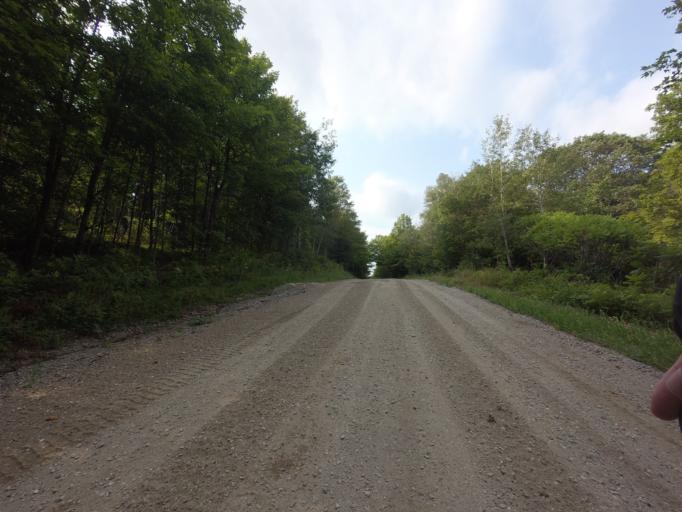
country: CA
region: Ontario
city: Perth
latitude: 44.8572
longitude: -76.7312
